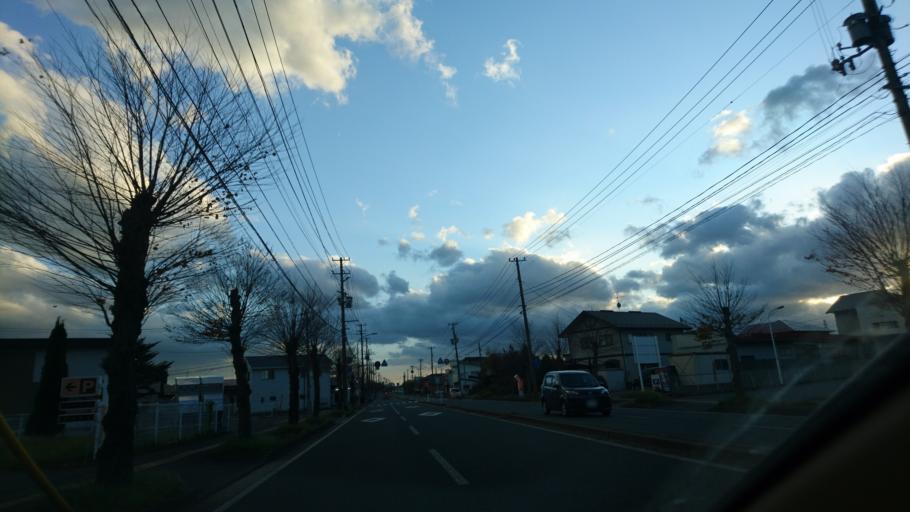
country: JP
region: Iwate
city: Mizusawa
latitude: 39.1505
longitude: 141.1326
